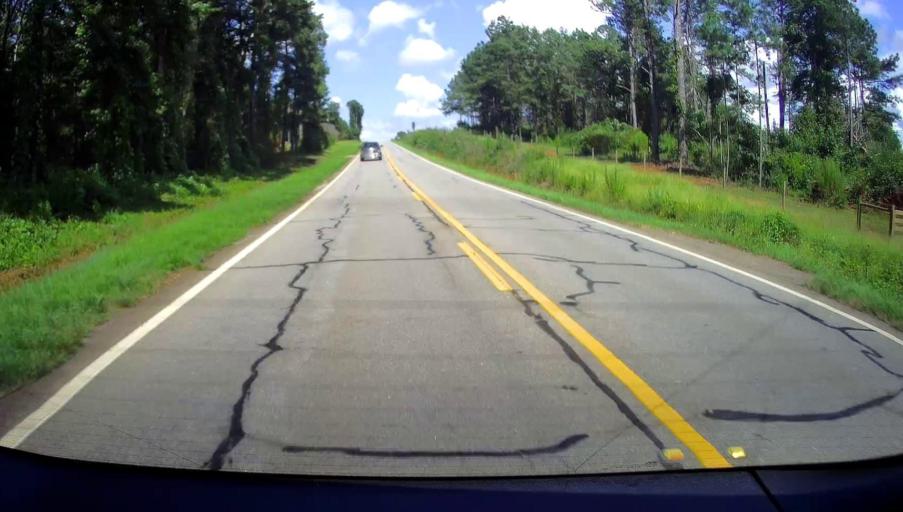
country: US
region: Georgia
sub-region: Upson County
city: Thomaston
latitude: 32.9161
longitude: -84.2567
